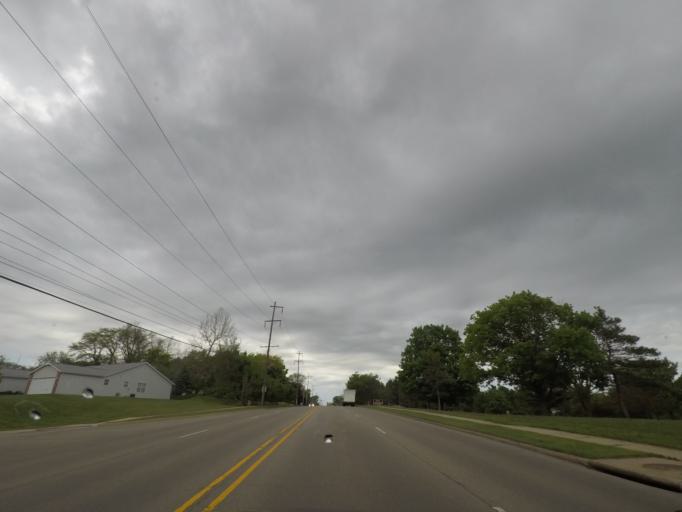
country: US
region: Illinois
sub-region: Winnebago County
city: Loves Park
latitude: 42.2718
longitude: -89.0290
